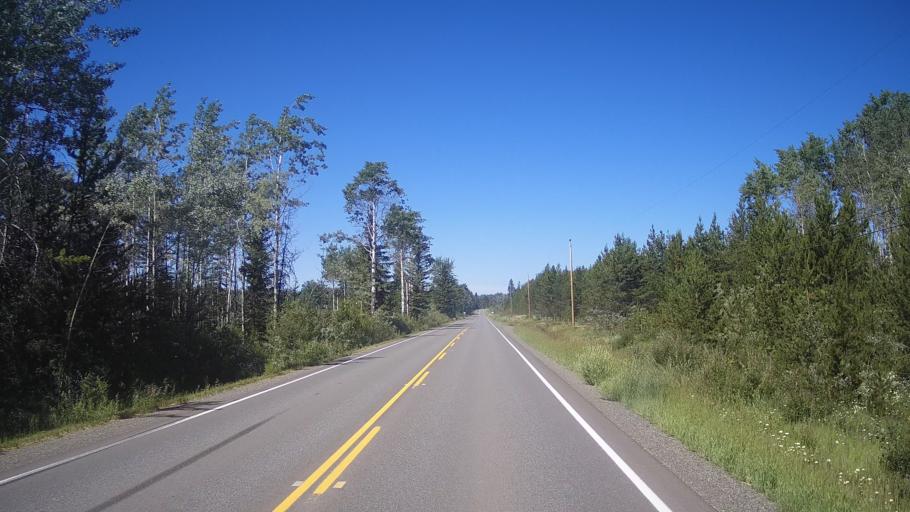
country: CA
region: British Columbia
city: Cache Creek
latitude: 51.5402
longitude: -121.0354
